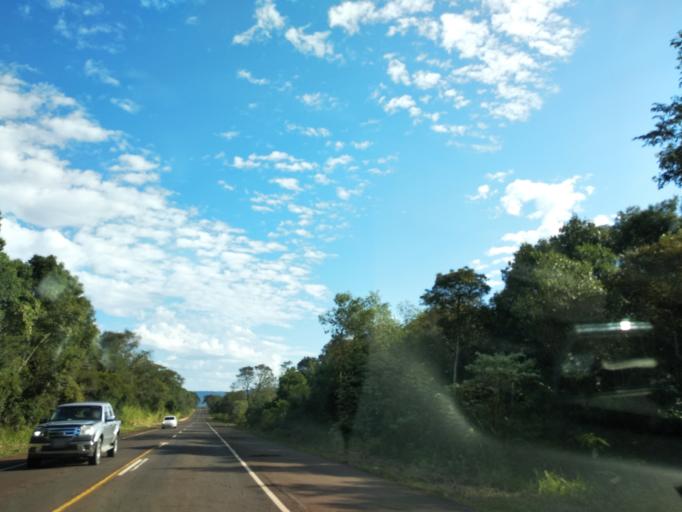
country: AR
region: Misiones
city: Aristobulo del Valle
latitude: -27.0937
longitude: -54.9521
